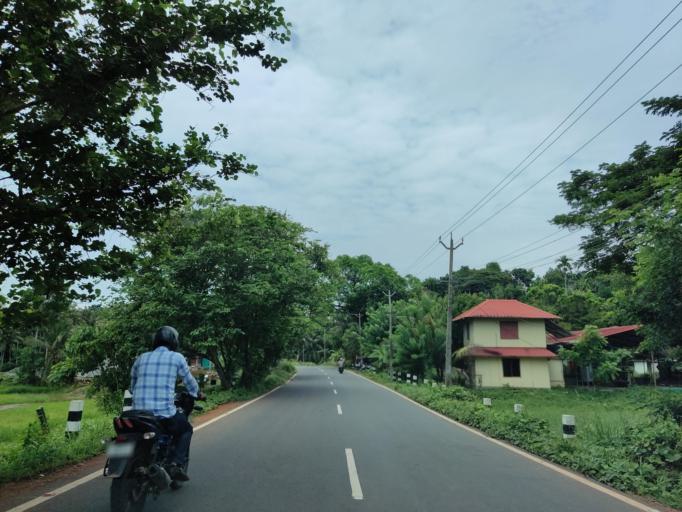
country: IN
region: Kerala
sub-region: Alappuzha
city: Mavelikara
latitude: 9.2676
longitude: 76.6048
